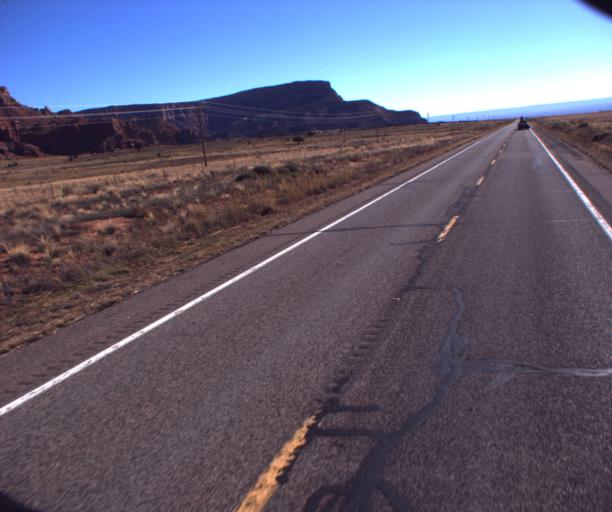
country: US
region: Arizona
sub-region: Mohave County
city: Colorado City
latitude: 36.8758
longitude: -112.8750
